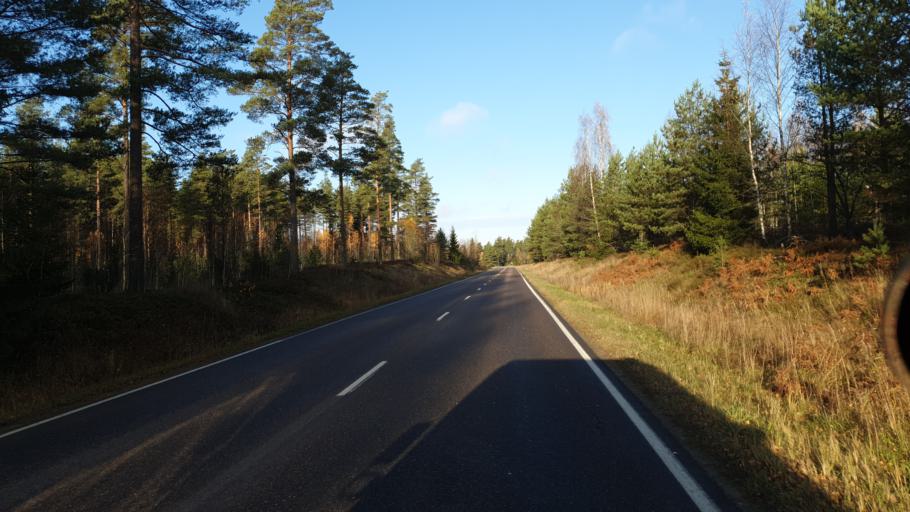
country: FI
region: Uusimaa
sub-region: Helsinki
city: Siuntio
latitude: 60.1952
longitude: 24.1946
